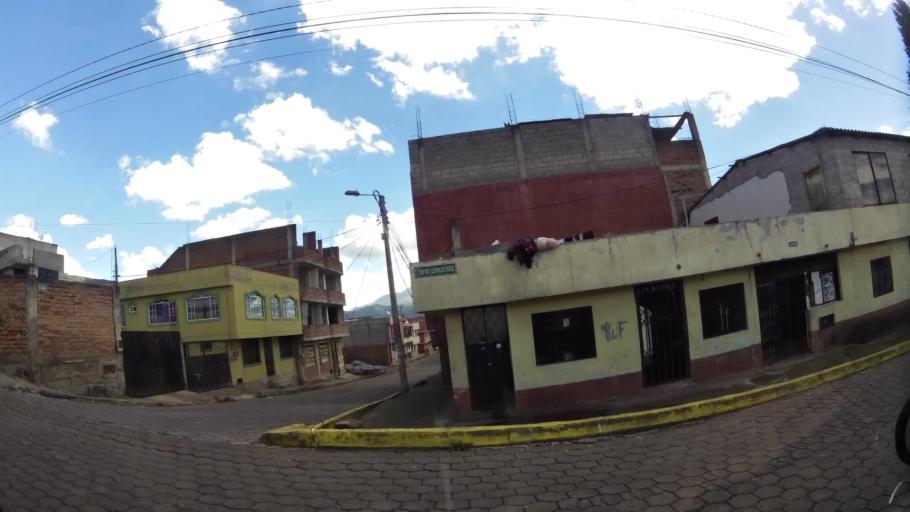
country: EC
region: Pichincha
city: Quito
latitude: -0.3265
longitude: -78.5578
